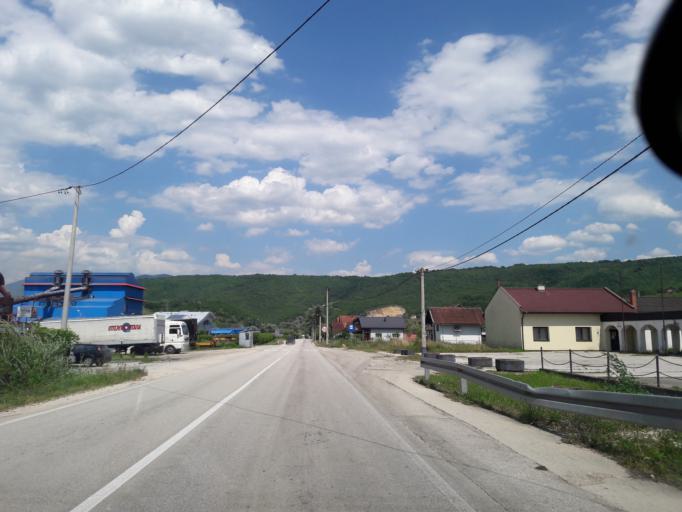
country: BA
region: Republika Srpska
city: Mrkonjic Grad
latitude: 44.4370
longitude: 17.1507
